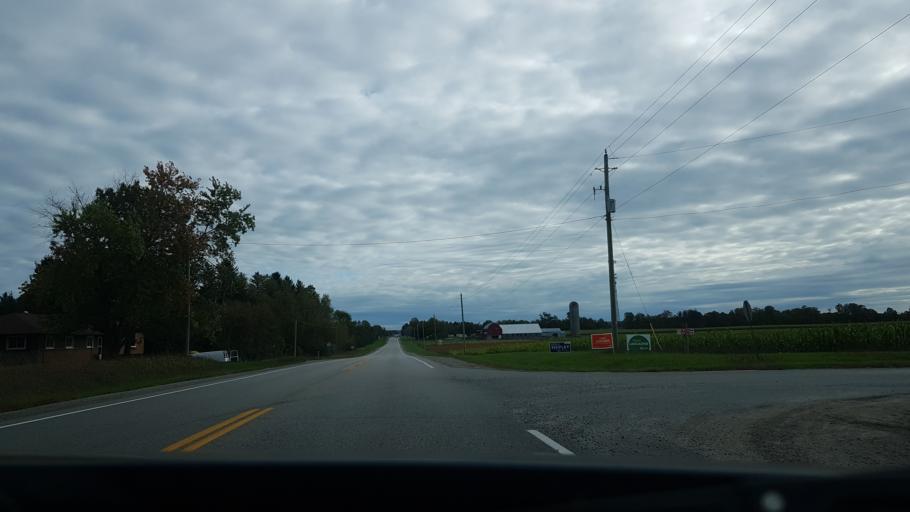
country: CA
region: Ontario
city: Barrie
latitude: 44.4938
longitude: -79.8045
